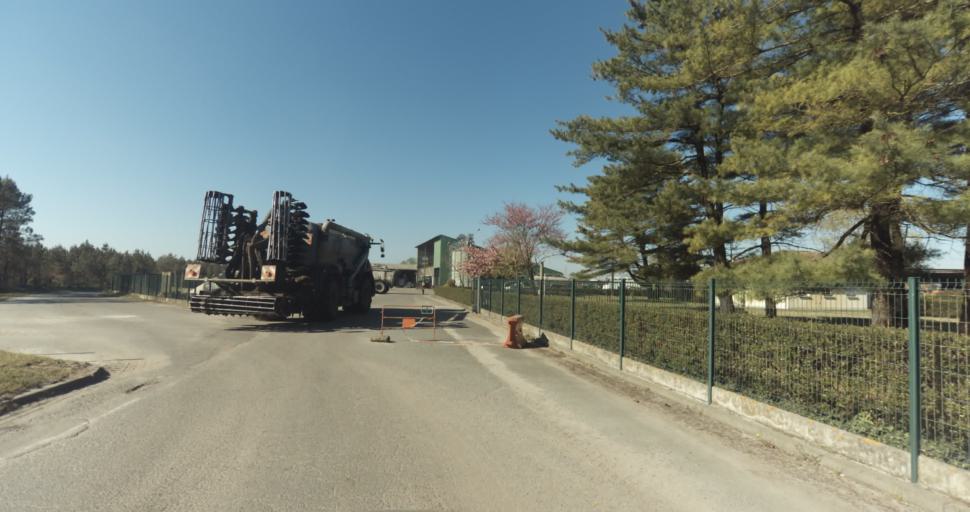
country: FR
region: Aquitaine
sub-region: Departement de la Gironde
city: Marcheprime
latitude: 44.7629
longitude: -0.8536
